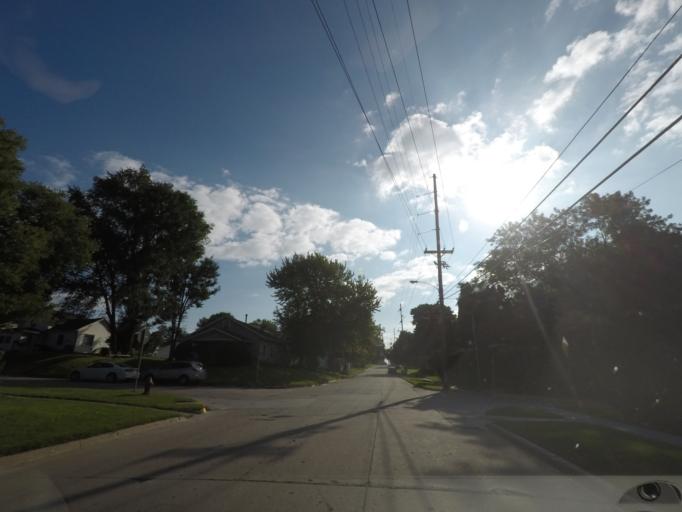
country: US
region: Iowa
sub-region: Story County
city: Nevada
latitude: 42.0156
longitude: -93.4539
